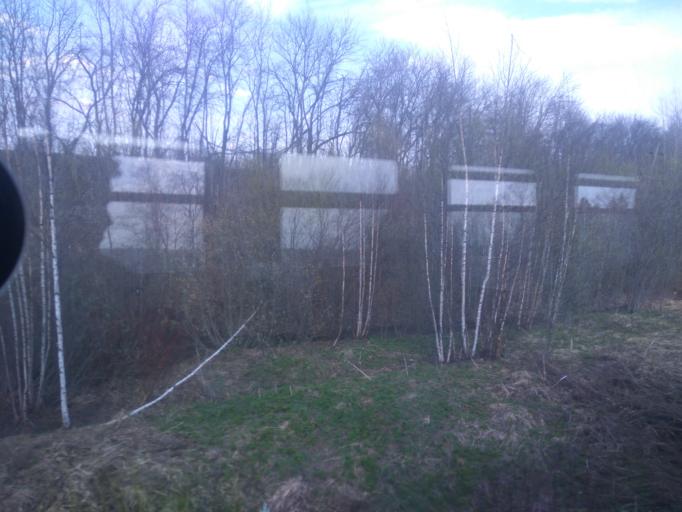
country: RU
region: Moskovskaya
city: Budenovetc
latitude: 56.3097
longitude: 37.6641
